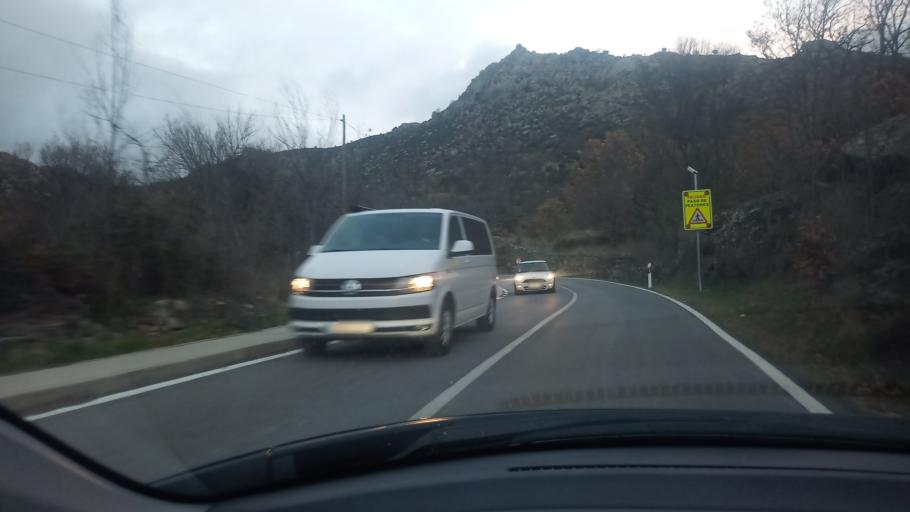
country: ES
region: Madrid
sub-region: Provincia de Madrid
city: Zarzalejo
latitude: 40.5447
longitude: -4.1725
